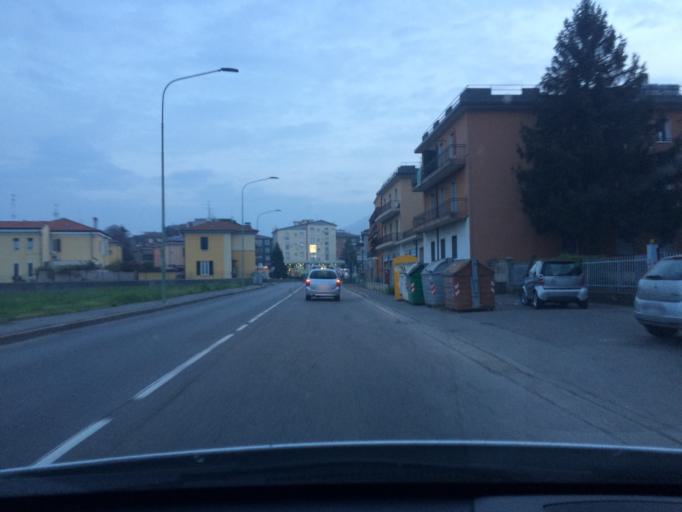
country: IT
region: Lombardy
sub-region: Provincia di Brescia
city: Brescia
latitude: 45.5217
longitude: 10.2297
